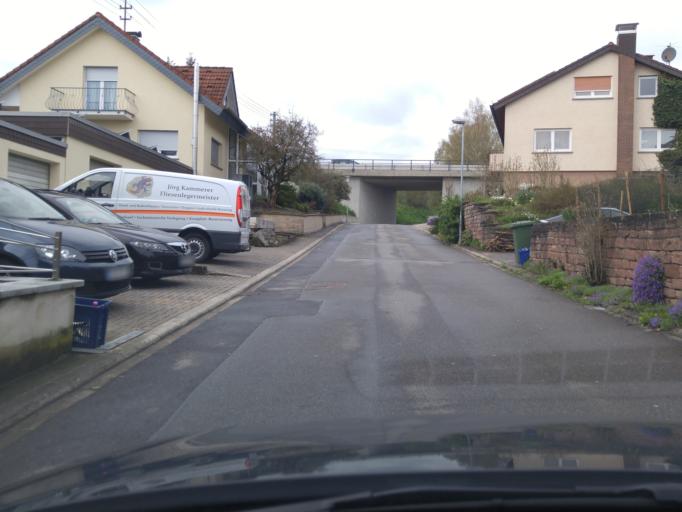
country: DE
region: Baden-Wuerttemberg
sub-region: Karlsruhe Region
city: Neckarbischofsheim
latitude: 49.3244
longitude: 8.9718
